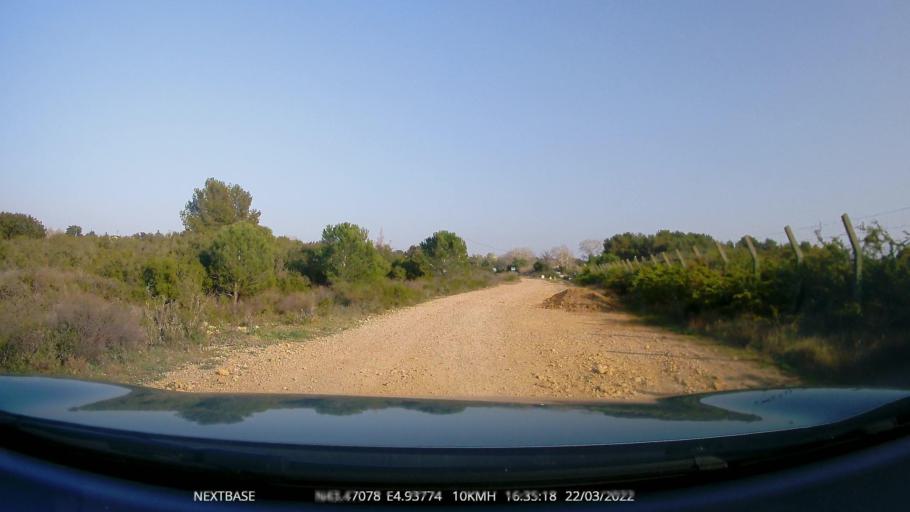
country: FR
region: Provence-Alpes-Cote d'Azur
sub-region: Departement des Bouches-du-Rhone
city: Fos-sur-Mer
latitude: 43.4710
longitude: 4.9378
